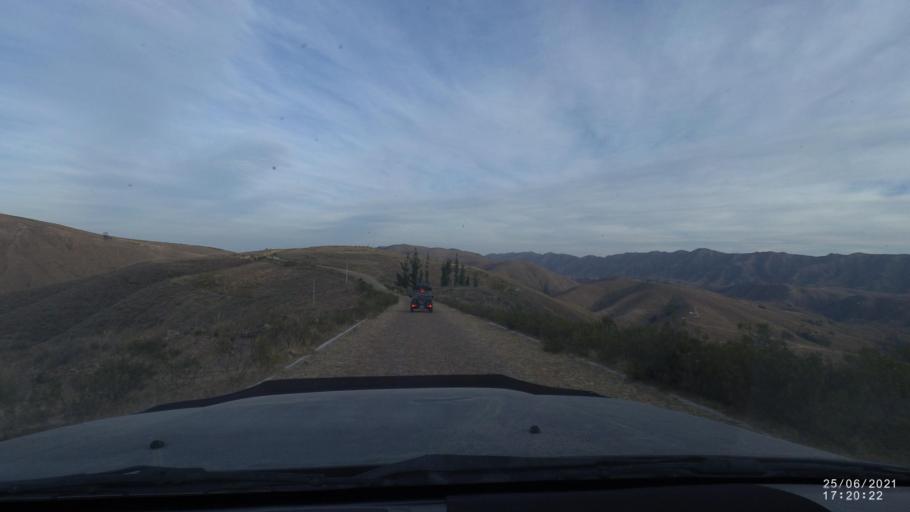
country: BO
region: Cochabamba
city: Arani
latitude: -17.9030
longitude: -65.6895
